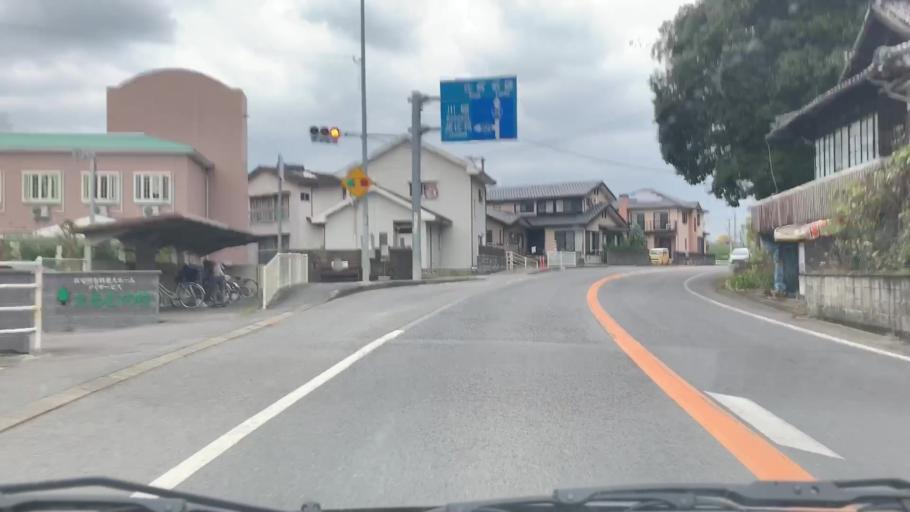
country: JP
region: Saga Prefecture
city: Ureshinomachi-shimojuku
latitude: 33.1355
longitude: 129.9877
